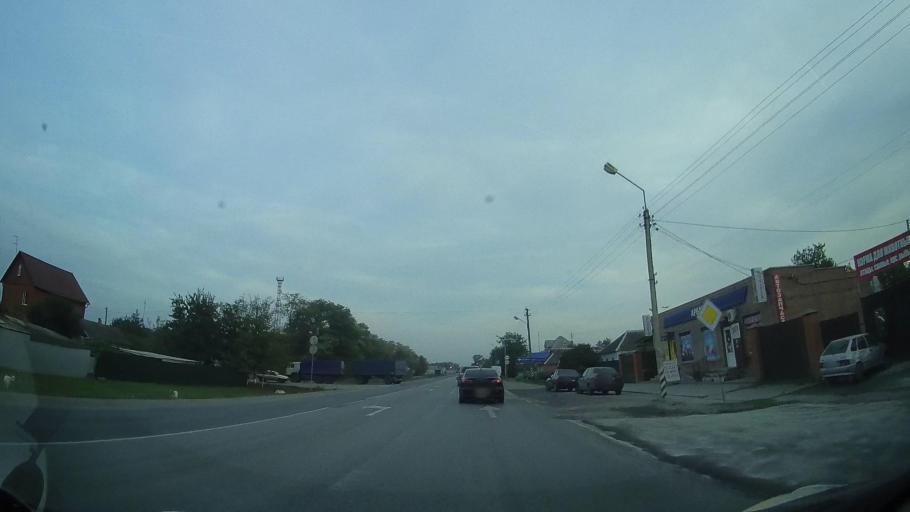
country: RU
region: Rostov
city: Kirovskaya
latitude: 46.9769
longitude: 40.0459
